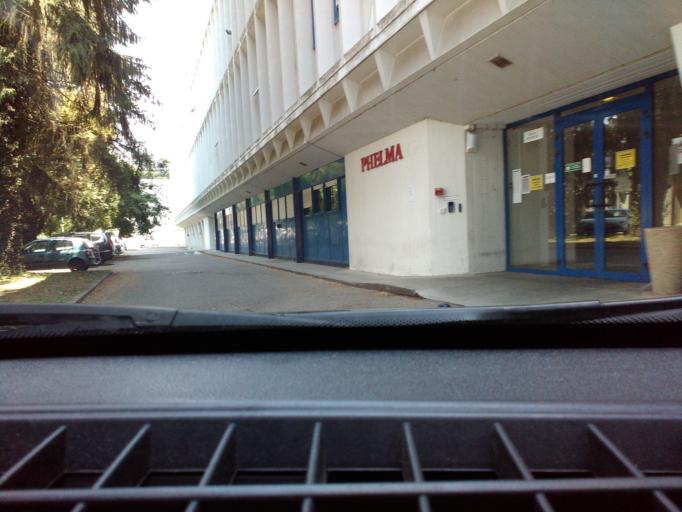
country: FR
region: Rhone-Alpes
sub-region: Departement de l'Isere
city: Corenc
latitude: 45.1956
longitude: 5.7705
